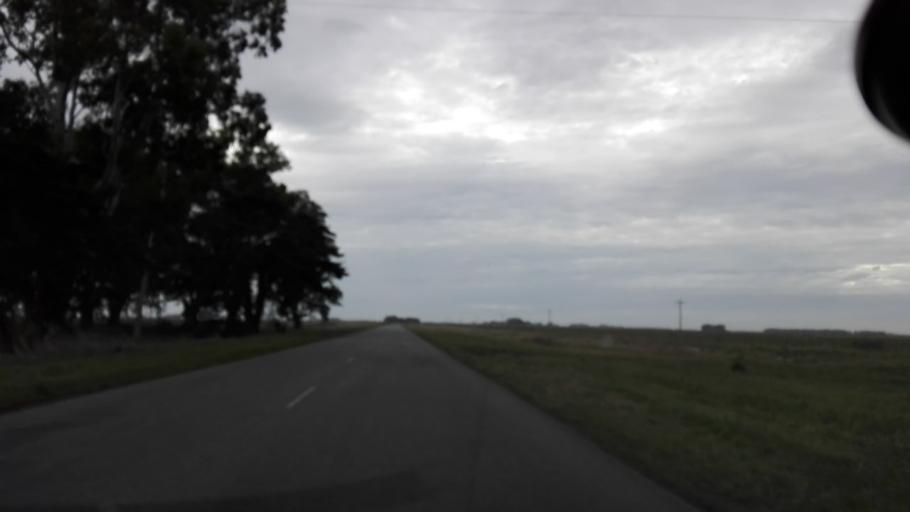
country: AR
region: Buenos Aires
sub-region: Partido de Rauch
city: Rauch
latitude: -36.5150
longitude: -59.0346
